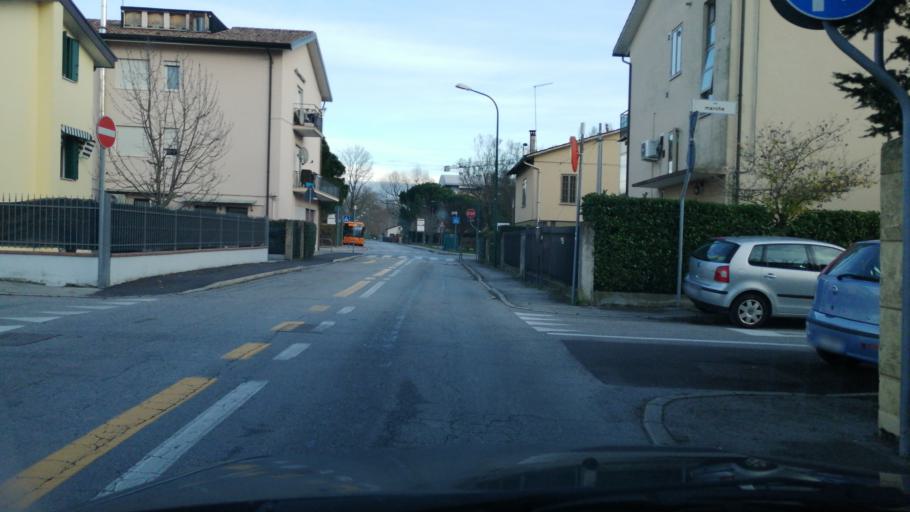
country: IT
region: Veneto
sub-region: Provincia di Venezia
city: Zelarino
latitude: 45.4909
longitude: 12.2111
